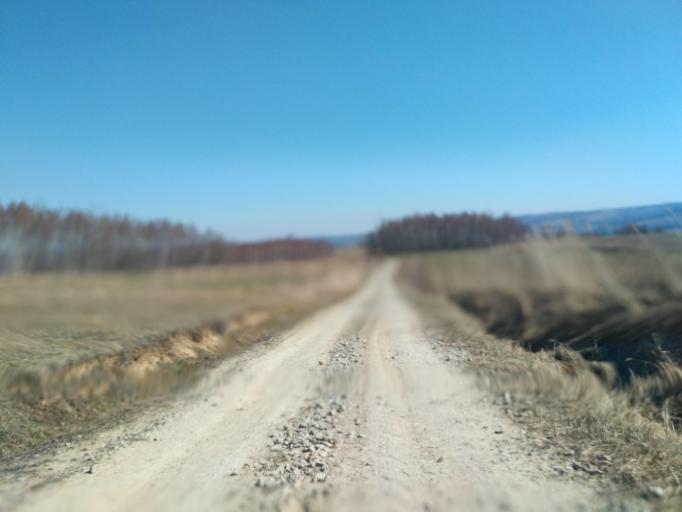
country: PL
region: Subcarpathian Voivodeship
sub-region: Powiat ropczycko-sedziszowski
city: Niedzwiada
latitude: 49.9538
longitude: 21.5572
